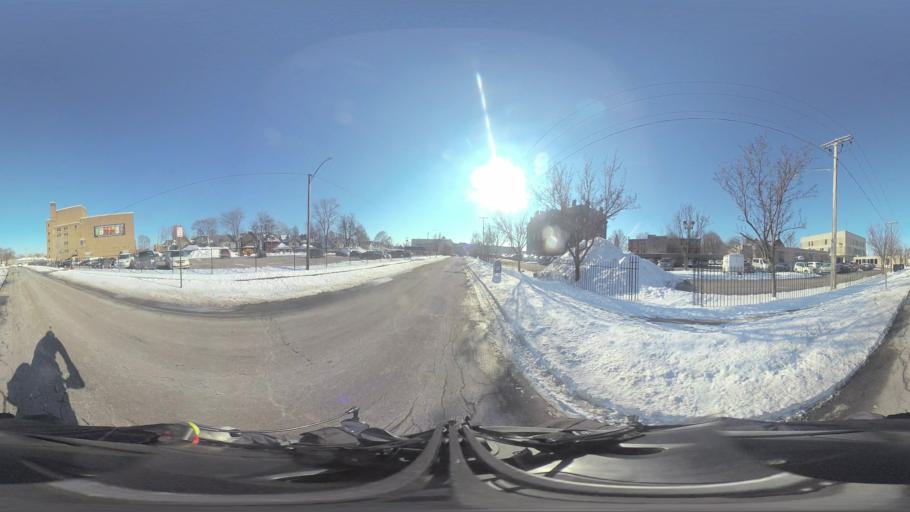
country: US
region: New York
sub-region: Monroe County
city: Rochester
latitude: 43.1596
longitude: -77.5879
